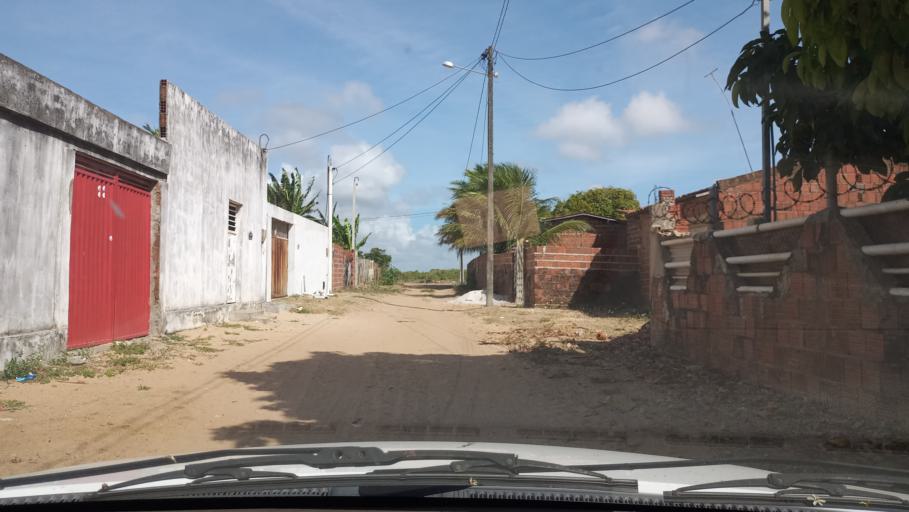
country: BR
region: Rio Grande do Norte
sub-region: Maxaranguape
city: Sao Miguel
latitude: -5.5140
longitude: -35.2654
